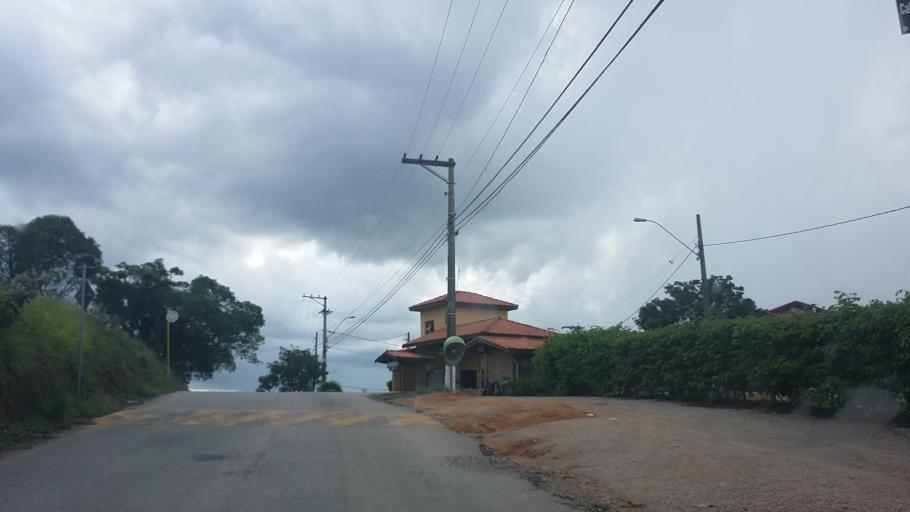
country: BR
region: Sao Paulo
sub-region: Itupeva
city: Itupeva
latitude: -23.1676
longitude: -47.0967
